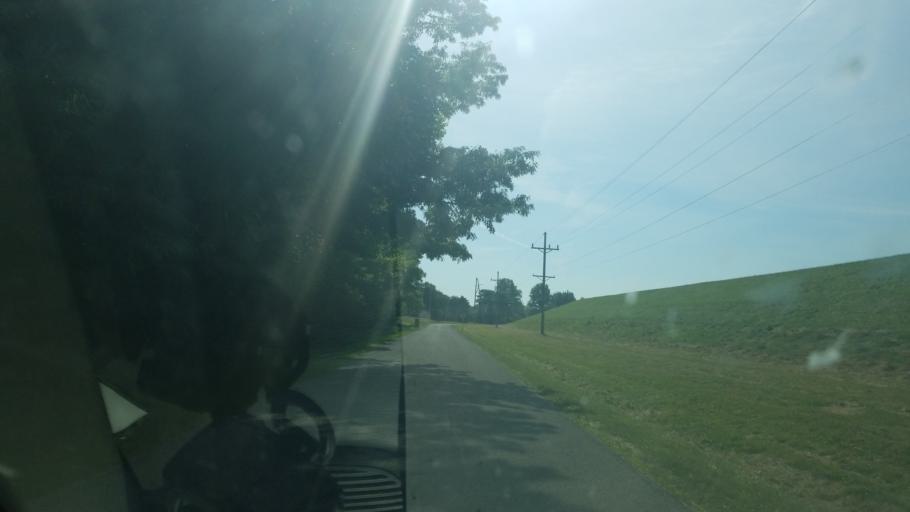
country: US
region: Ohio
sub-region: Hancock County
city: Findlay
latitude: 41.0288
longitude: -83.5693
